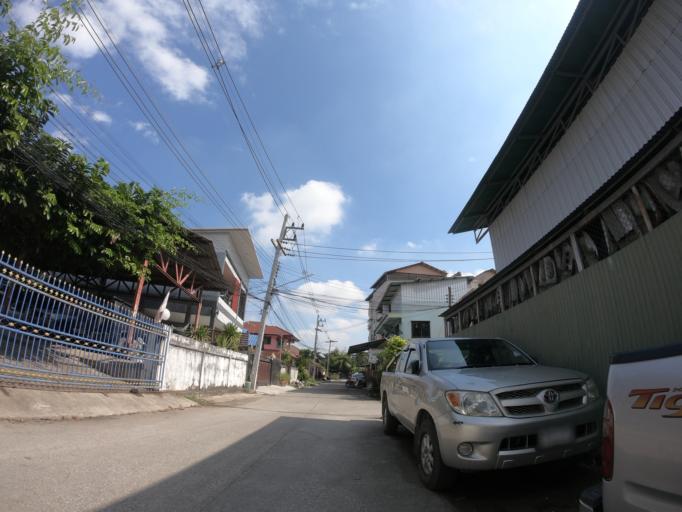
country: TH
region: Chiang Mai
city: Chiang Mai
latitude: 18.7726
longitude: 98.9867
